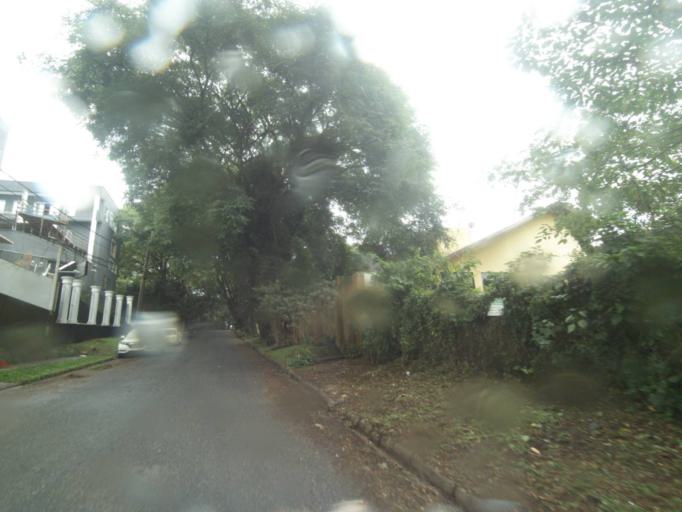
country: BR
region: Parana
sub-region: Curitiba
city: Curitiba
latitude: -25.4236
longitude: -49.3144
